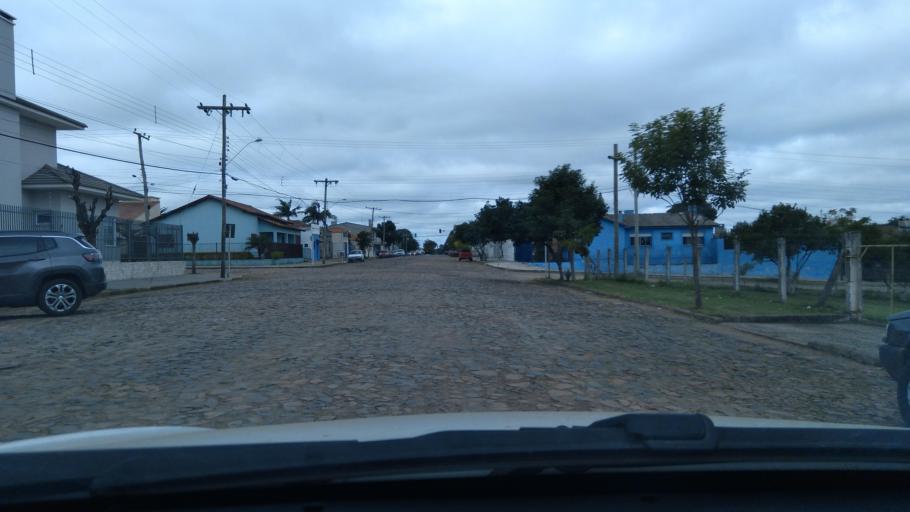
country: BR
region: Rio Grande do Sul
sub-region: Dom Pedrito
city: Dom Pedrito
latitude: -30.9739
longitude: -54.6761
